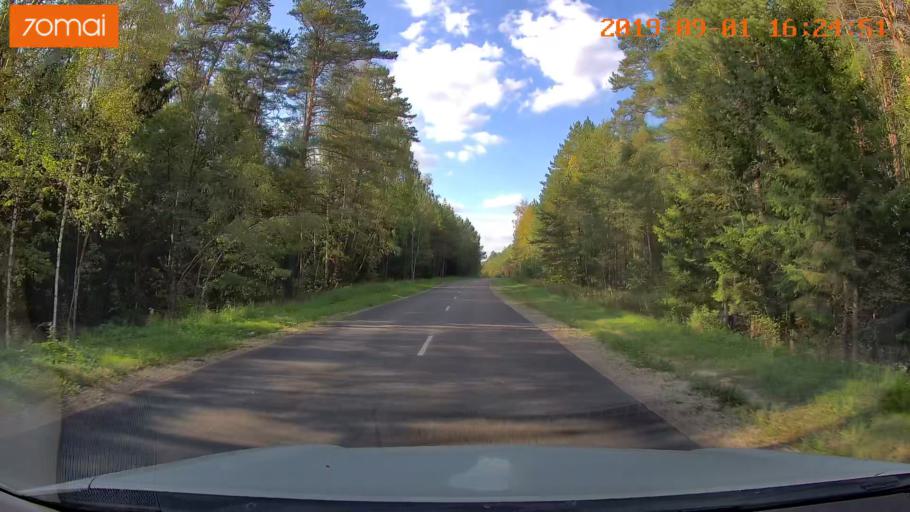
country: RU
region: Kaluga
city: Maloyaroslavets
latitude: 54.8956
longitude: 36.5194
